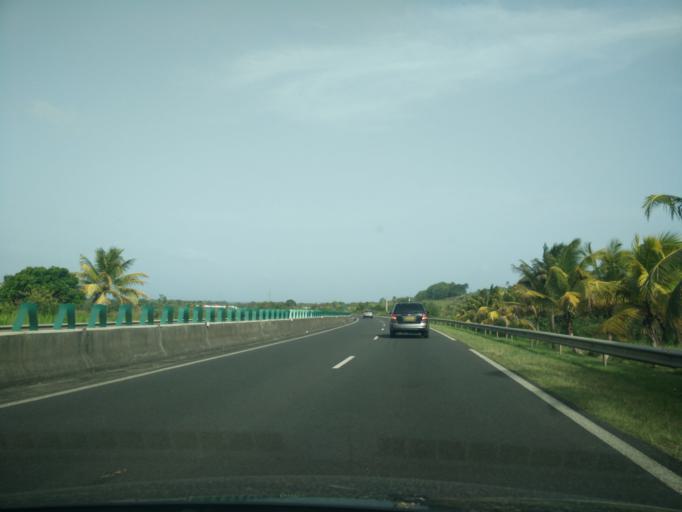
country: GP
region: Guadeloupe
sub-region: Guadeloupe
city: Petit-Bourg
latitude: 16.1837
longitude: -61.6053
